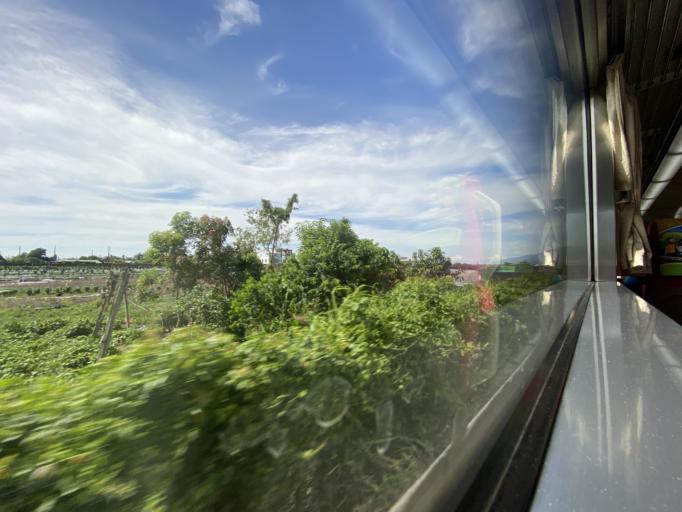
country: TW
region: Taiwan
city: Taitung City
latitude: 22.6843
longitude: 121.0462
